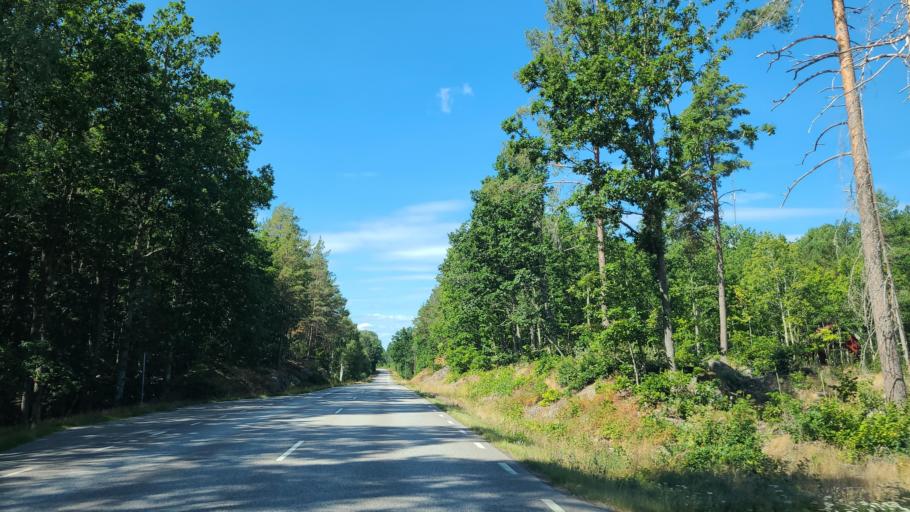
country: SE
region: Kalmar
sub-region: Nybro Kommun
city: Nybro
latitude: 56.5641
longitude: 15.8024
